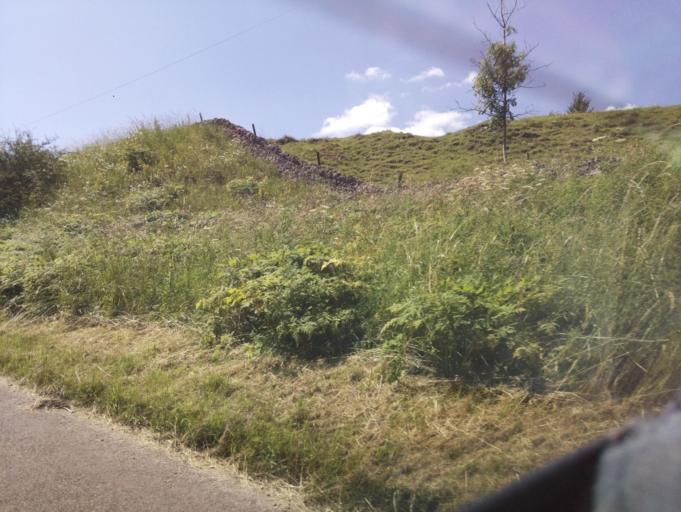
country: GB
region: England
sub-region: Derbyshire
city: Buxton
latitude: 53.2173
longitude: -1.8725
